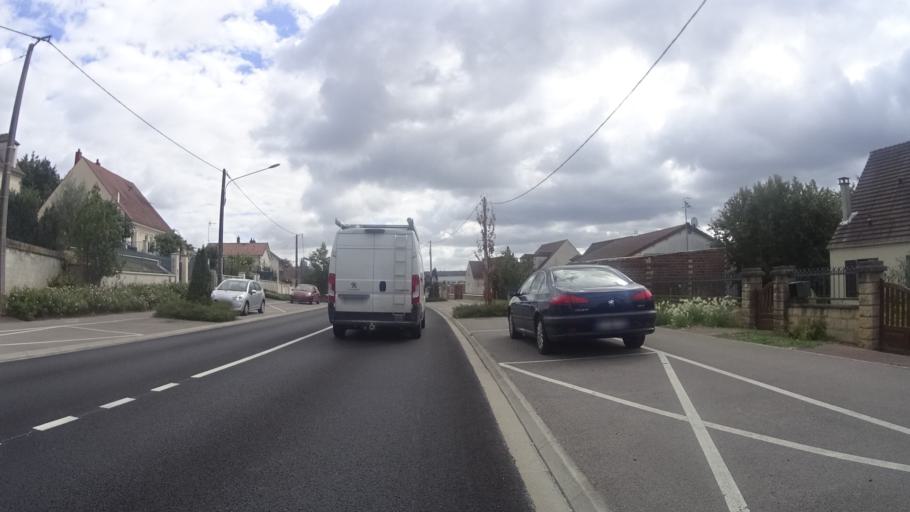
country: FR
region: Picardie
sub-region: Departement de l'Oise
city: Clairoix
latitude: 49.4403
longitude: 2.8548
